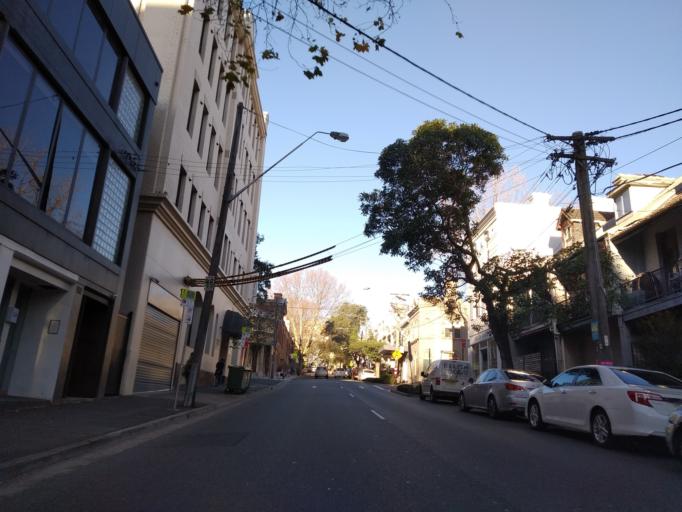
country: AU
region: New South Wales
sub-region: City of Sydney
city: Haymarket
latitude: -33.8824
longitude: 151.2102
